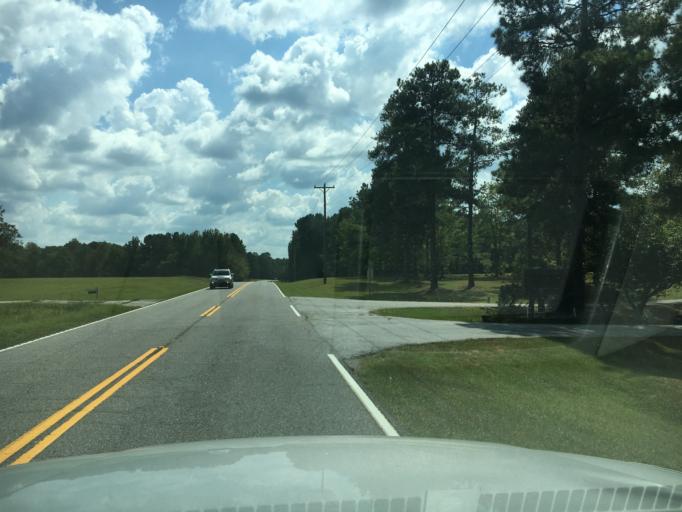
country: US
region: South Carolina
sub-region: Greenwood County
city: Greenwood
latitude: 34.1040
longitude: -82.1299
